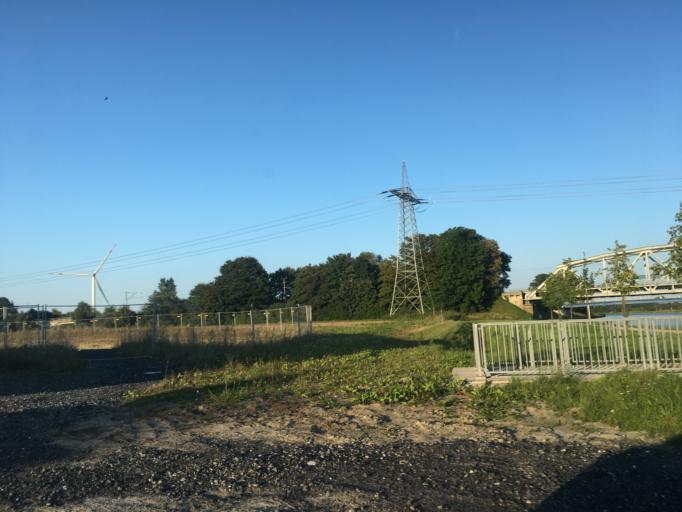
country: DE
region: North Rhine-Westphalia
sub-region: Regierungsbezirk Munster
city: Muenster
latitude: 51.8883
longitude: 7.5967
